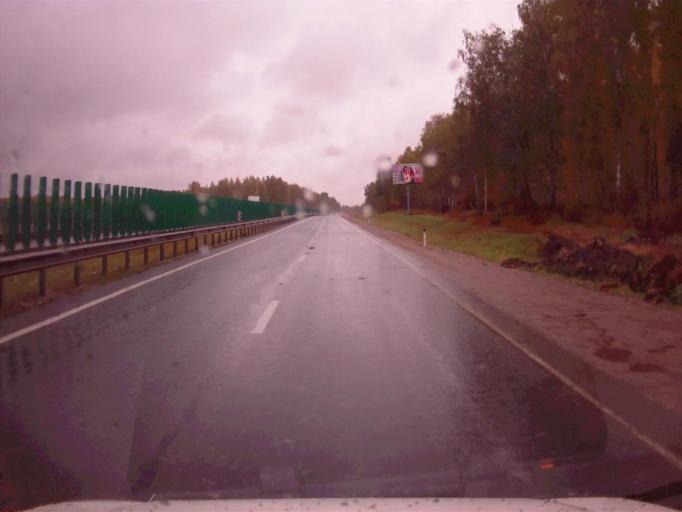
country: RU
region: Chelyabinsk
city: Dolgoderevenskoye
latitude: 55.3317
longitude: 61.3184
